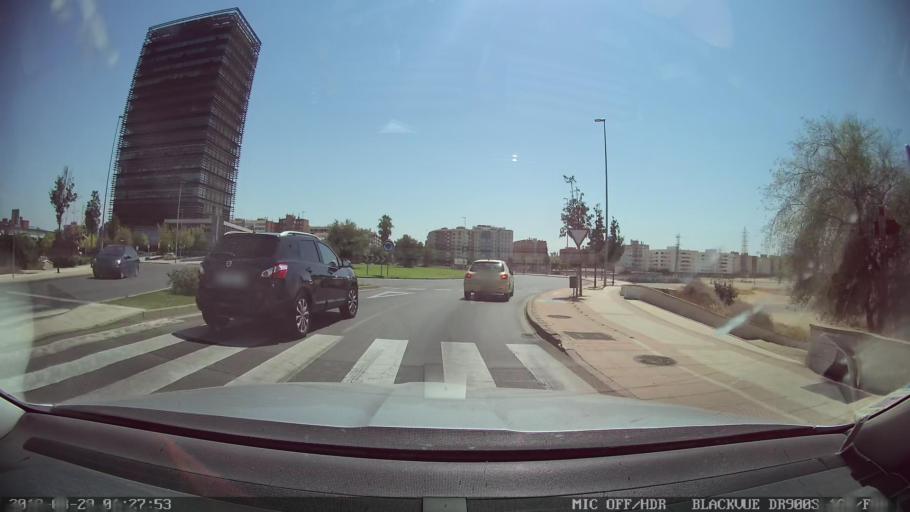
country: ES
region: Extremadura
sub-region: Provincia de Badajoz
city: Badajoz
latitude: 38.8742
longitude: -6.9932
